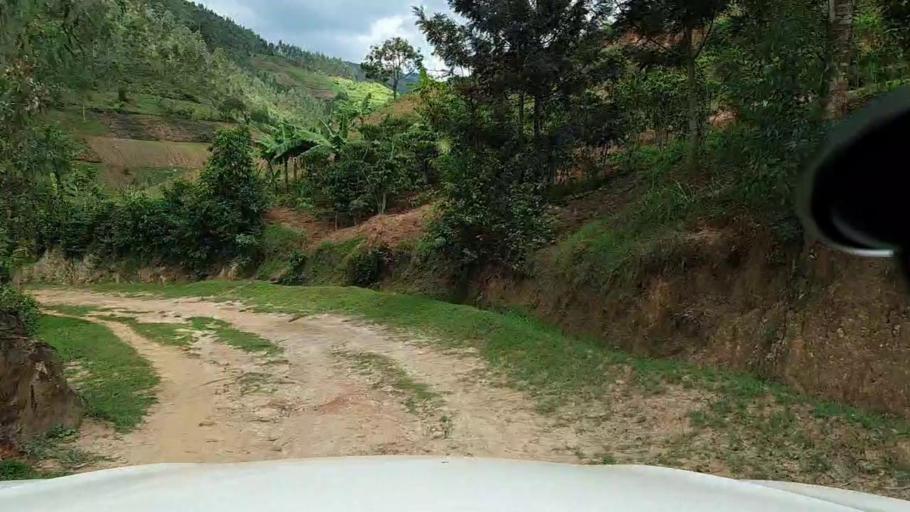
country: RW
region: Southern Province
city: Gitarama
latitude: -1.8152
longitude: 29.8012
